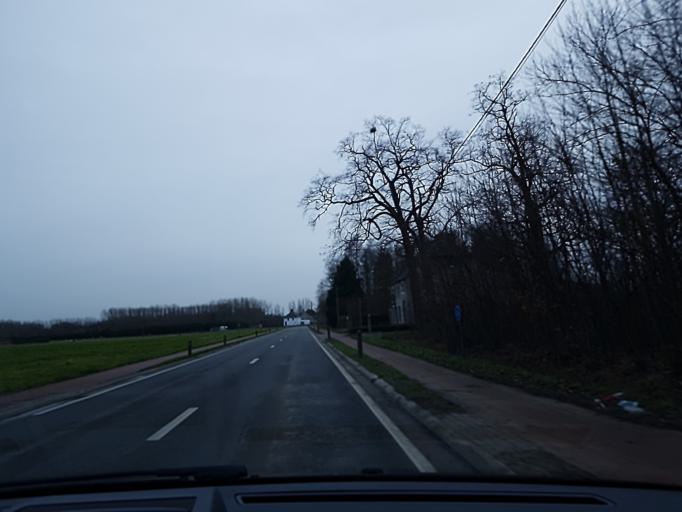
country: BE
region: Flanders
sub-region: Provincie Antwerpen
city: Putte
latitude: 51.0368
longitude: 4.6343
